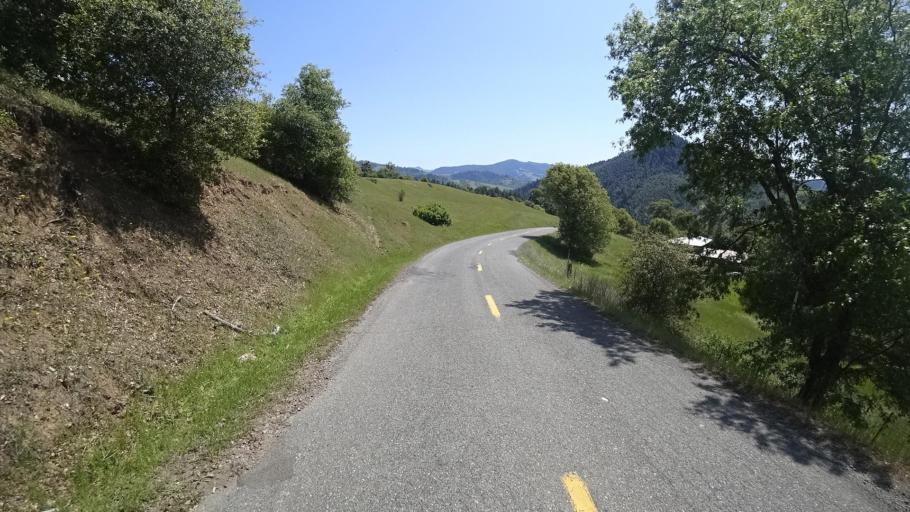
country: US
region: California
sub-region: Humboldt County
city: Redway
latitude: 40.2389
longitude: -123.6226
